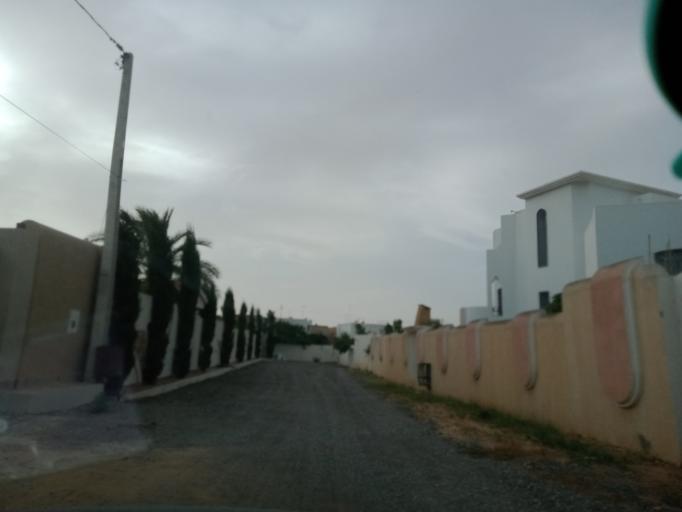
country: TN
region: Safaqis
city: Al Qarmadah
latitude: 34.8053
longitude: 10.7546
